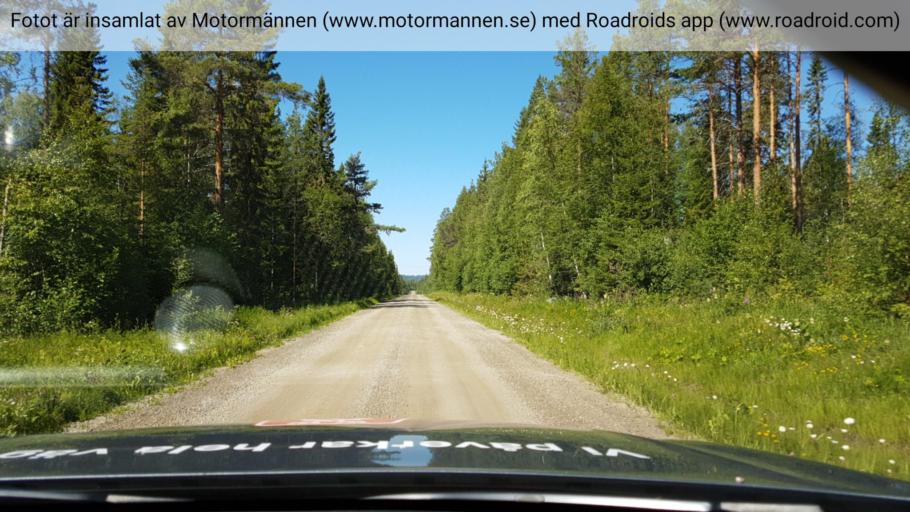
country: SE
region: Jaemtland
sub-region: Braecke Kommun
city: Braecke
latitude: 62.7984
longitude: 15.2540
